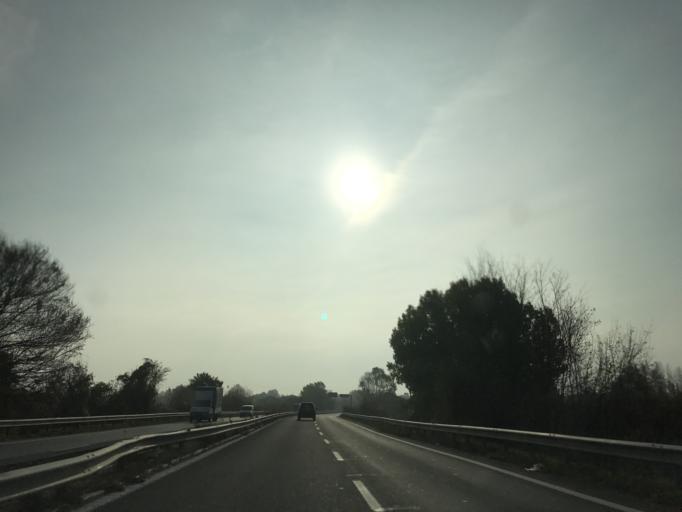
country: IT
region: Emilia-Romagna
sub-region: Provincia di Rimini
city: Bellaria-Igea Marina
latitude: 44.1450
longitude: 12.4530
